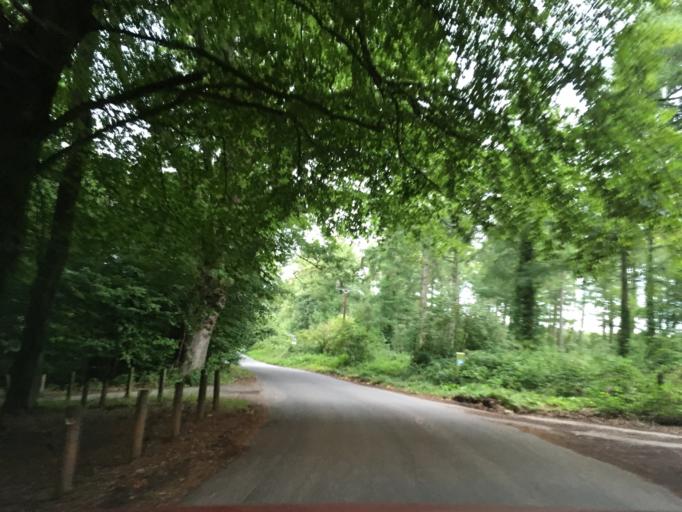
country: GB
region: Wales
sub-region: Newport
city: Llanvaches
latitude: 51.6411
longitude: -2.8269
